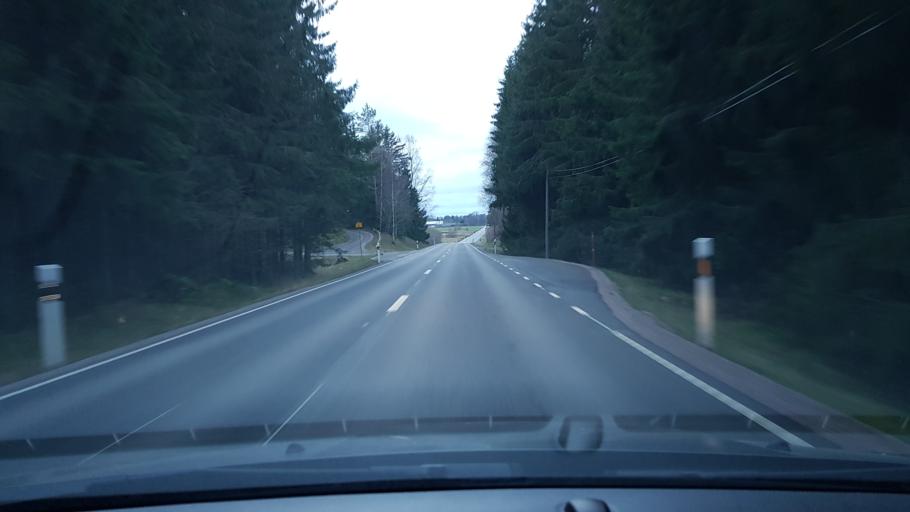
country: SE
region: Uppsala
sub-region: Uppsala Kommun
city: Vattholma
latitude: 59.9488
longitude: 17.9365
